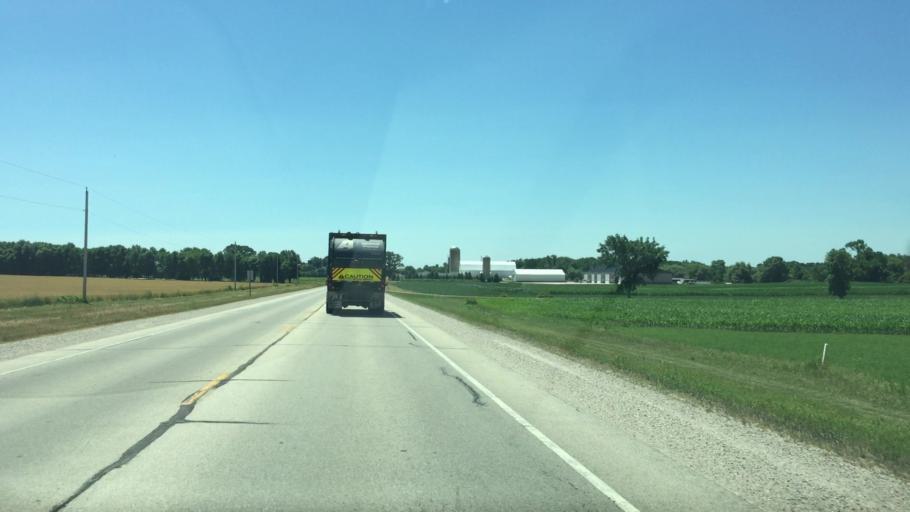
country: US
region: Wisconsin
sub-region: Calumet County
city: Chilton
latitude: 44.0710
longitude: -88.1633
